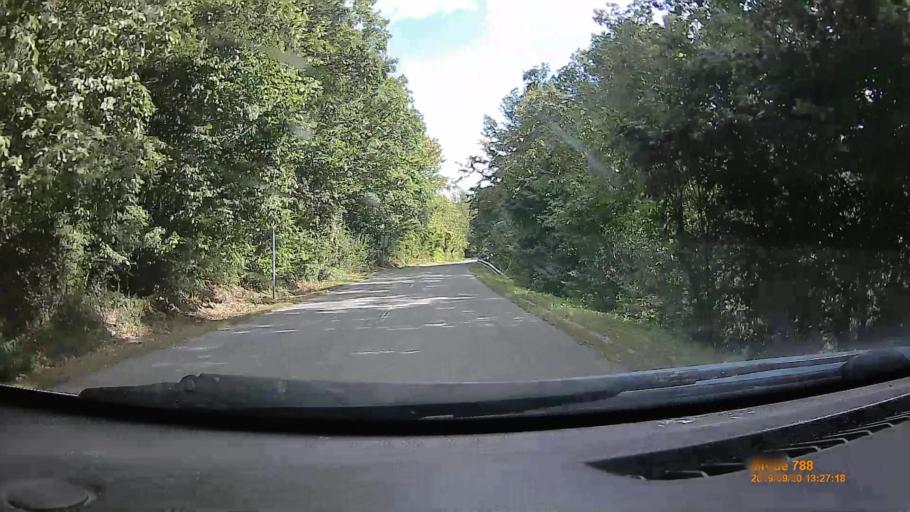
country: HU
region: Heves
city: Felsotarkany
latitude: 48.0430
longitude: 20.4906
